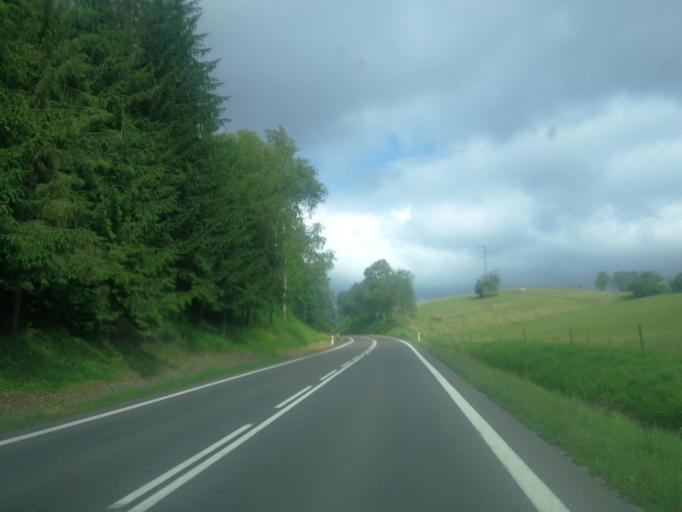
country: PL
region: Subcarpathian Voivodeship
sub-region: Powiat leski
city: Lesko
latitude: 49.4973
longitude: 22.3063
